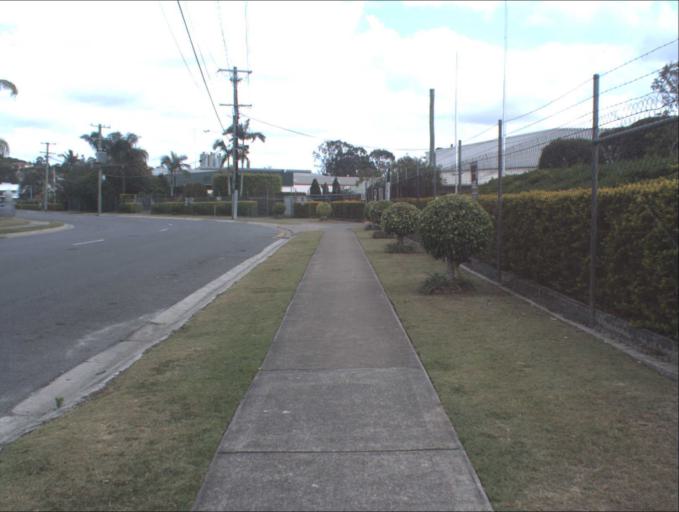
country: AU
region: Queensland
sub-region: Logan
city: Springwood
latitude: -27.6149
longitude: 153.1170
